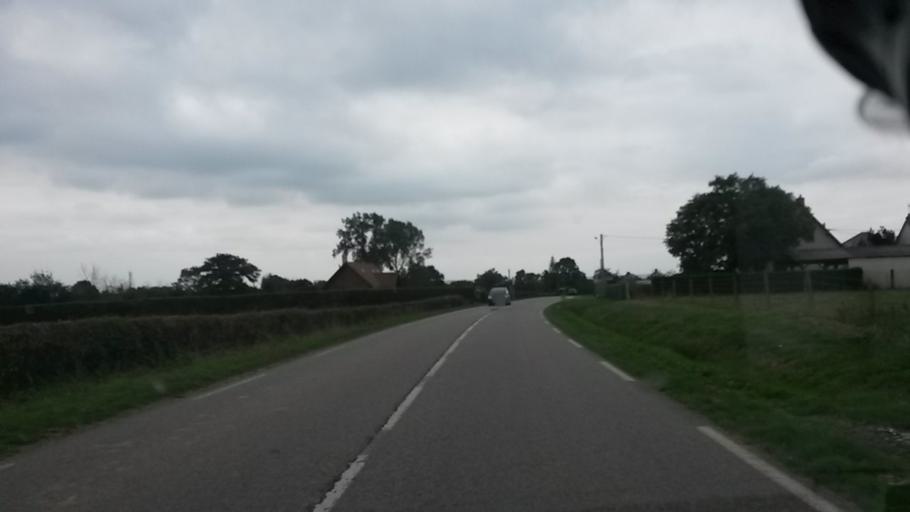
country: FR
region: Haute-Normandie
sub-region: Departement de la Seine-Maritime
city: Gaillefontaine
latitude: 49.6351
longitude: 1.5913
